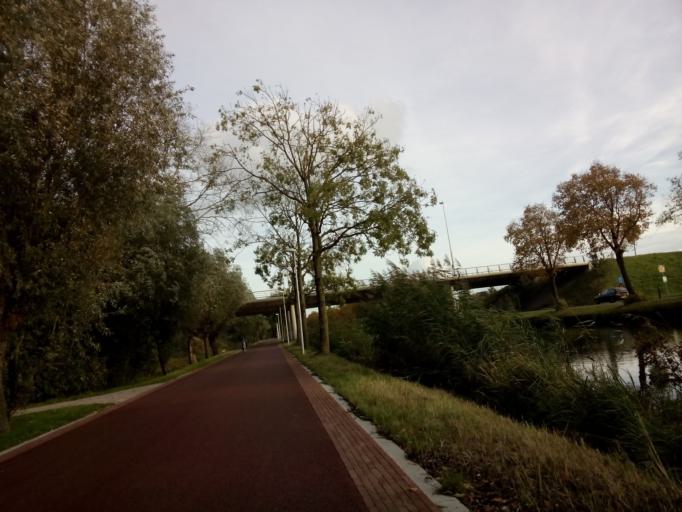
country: NL
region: Utrecht
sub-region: Stichtse Vecht
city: Spechtenkamp
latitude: 52.0889
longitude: 5.0030
